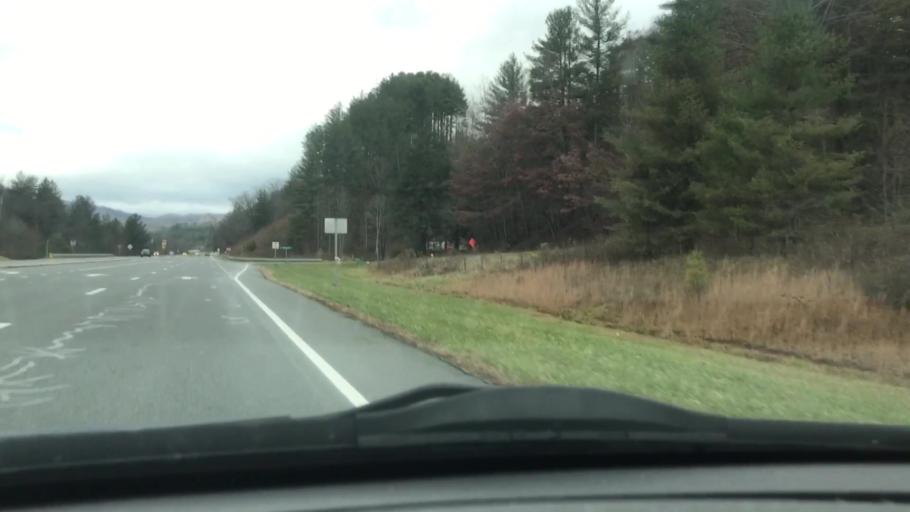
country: US
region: North Carolina
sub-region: Yancey County
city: Burnsville
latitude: 35.9136
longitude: -82.4109
